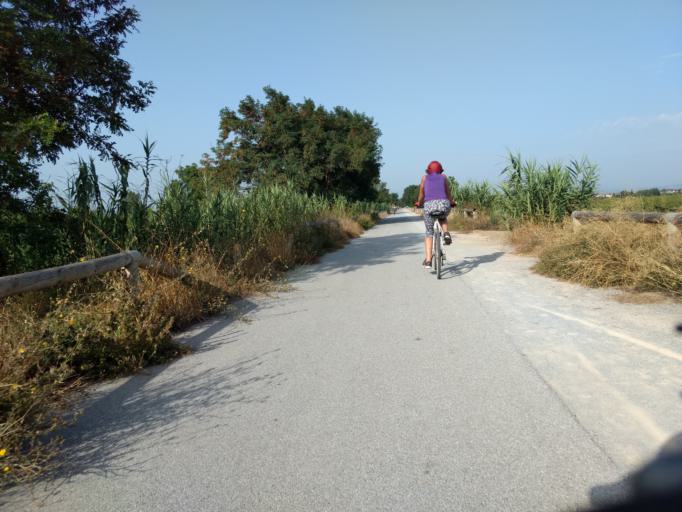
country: FR
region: Languedoc-Roussillon
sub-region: Departement des Pyrenees-Orientales
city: Saint-Laurent-de-la-Salanque
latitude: 42.7628
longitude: 2.9815
